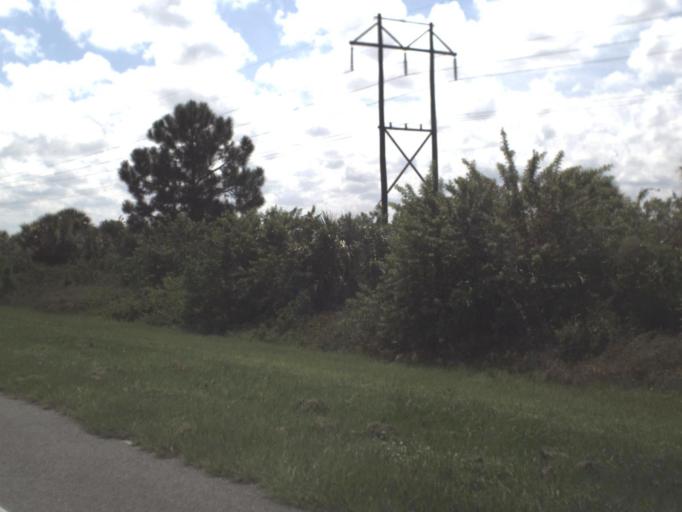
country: US
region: Florida
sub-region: Collier County
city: Immokalee
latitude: 26.3778
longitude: -81.3634
